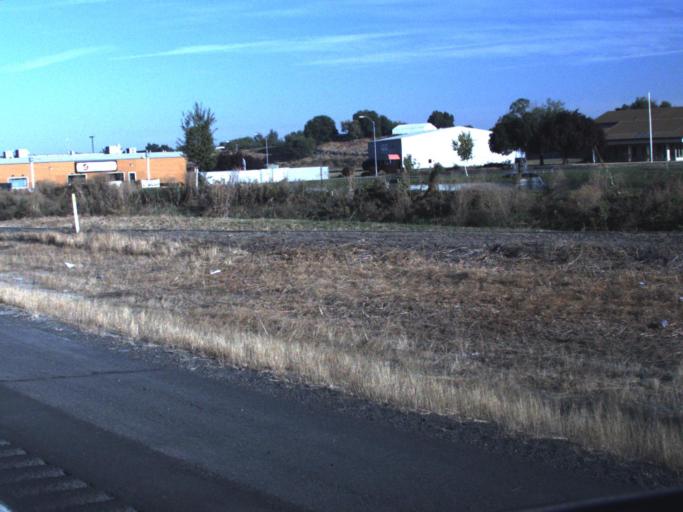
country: US
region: Washington
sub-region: Yakima County
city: Zillah
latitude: 46.4048
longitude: -120.2821
